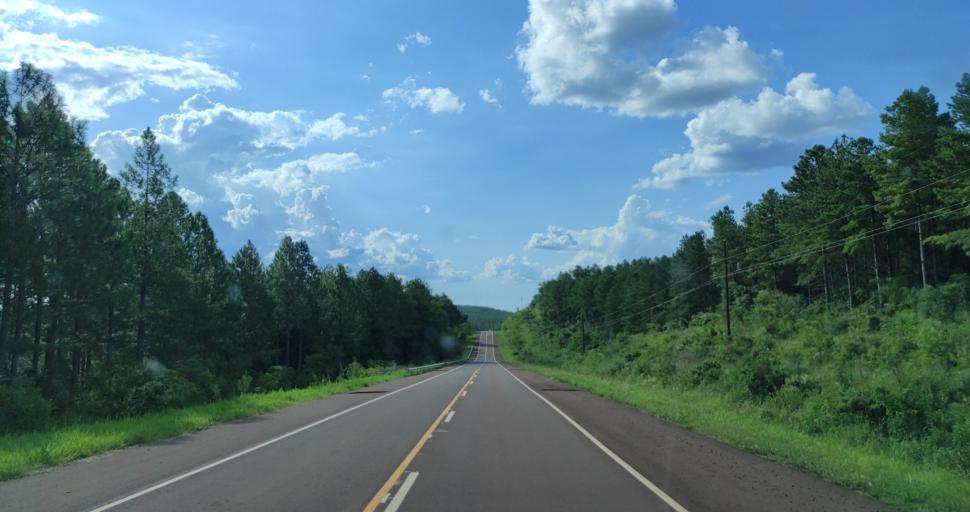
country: AR
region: Misiones
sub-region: Departamento de San Pedro
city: San Pedro
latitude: -26.3602
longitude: -53.9529
